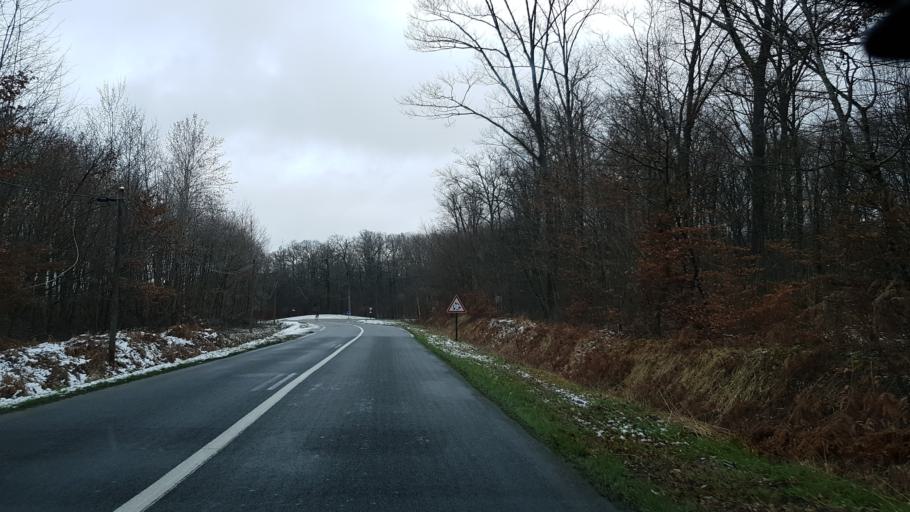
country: FR
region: Rhone-Alpes
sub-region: Departement de l'Ain
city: Peronnas
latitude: 46.1755
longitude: 5.2329
